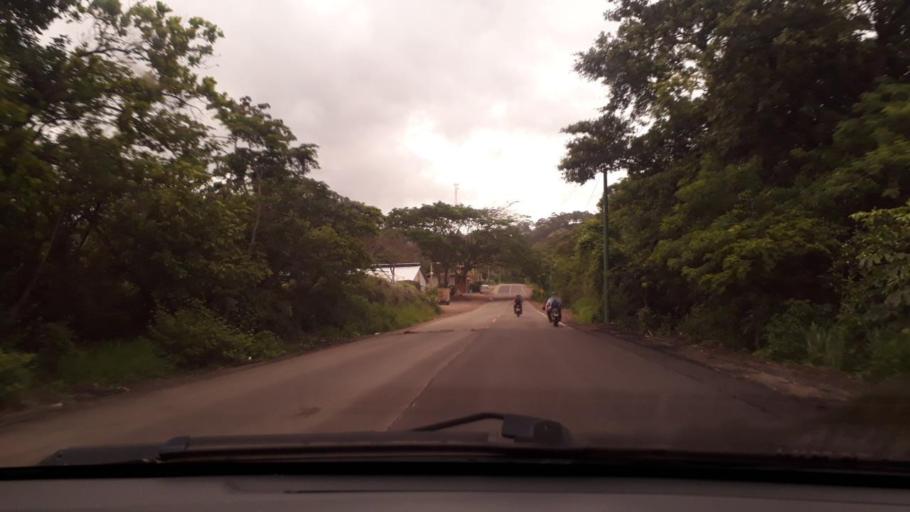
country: GT
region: Chiquimula
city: Concepcion Las Minas
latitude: 14.5355
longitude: -89.4633
